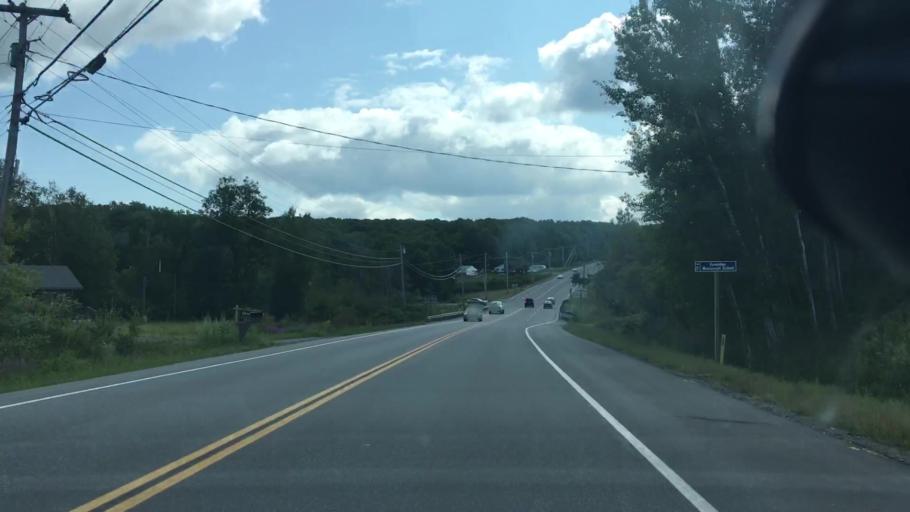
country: US
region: Maine
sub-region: Kennebec County
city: Waterville
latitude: 44.6001
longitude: -69.6565
